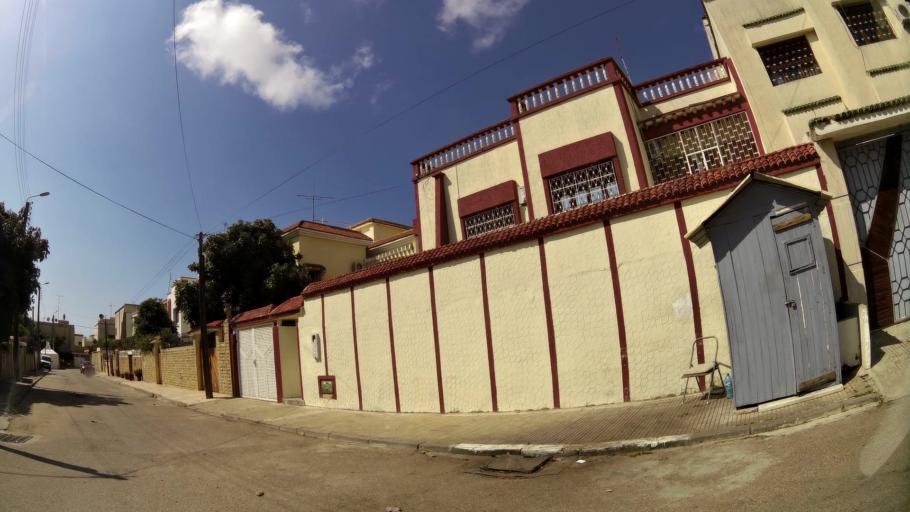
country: MA
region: Rabat-Sale-Zemmour-Zaer
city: Sale
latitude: 34.0373
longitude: -6.7893
